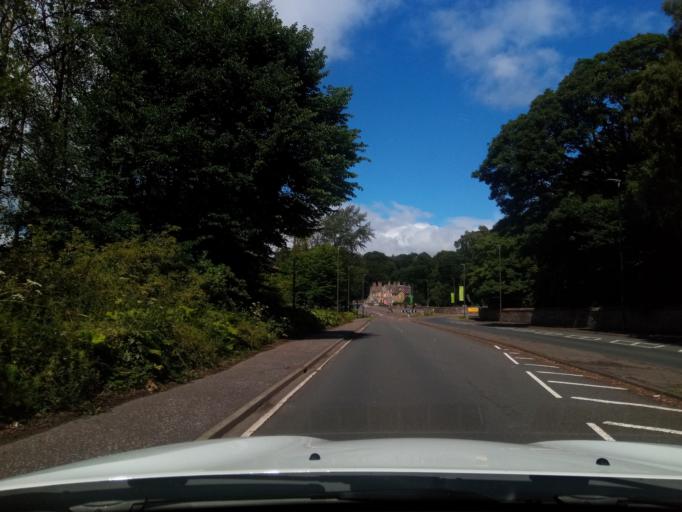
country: GB
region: Scotland
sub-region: Stirling
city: Bridge of Allan
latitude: 56.1463
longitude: -3.9284
